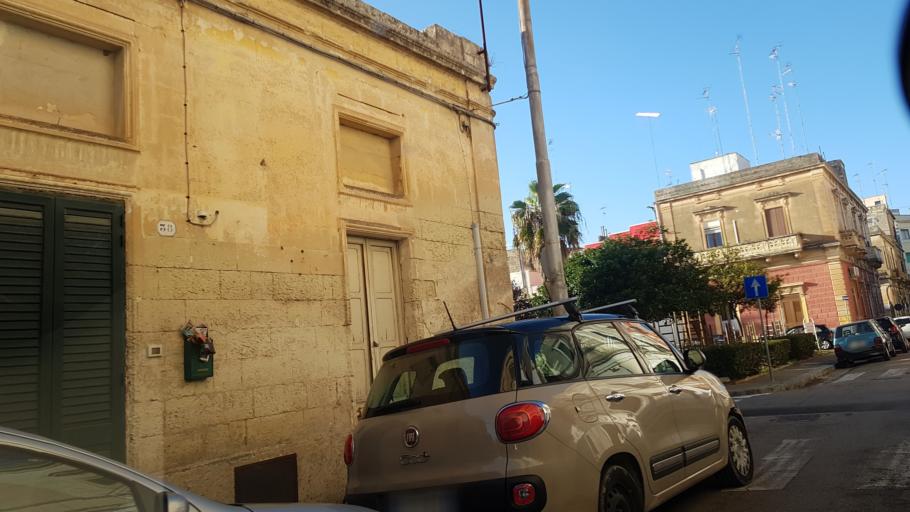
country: IT
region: Apulia
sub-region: Provincia di Lecce
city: Lecce
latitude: 40.3504
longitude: 18.1599
